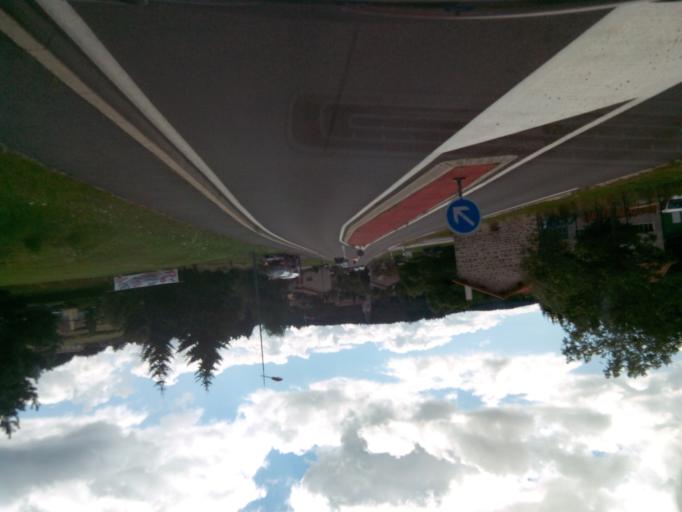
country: FR
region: Rhone-Alpes
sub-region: Departement de la Loire
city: Saint-Bonnet-le-Chateau
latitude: 45.4192
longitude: 4.0166
